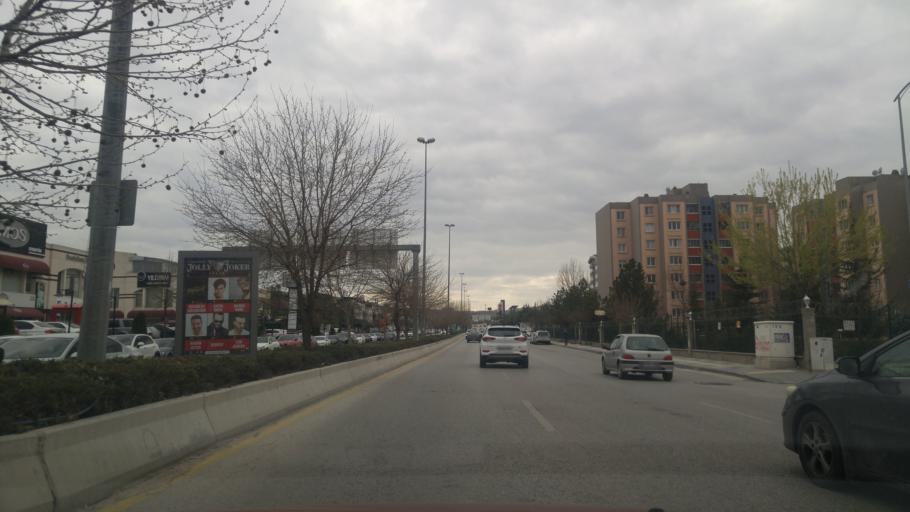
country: TR
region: Ankara
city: Etimesgut
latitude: 39.8727
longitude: 32.6879
